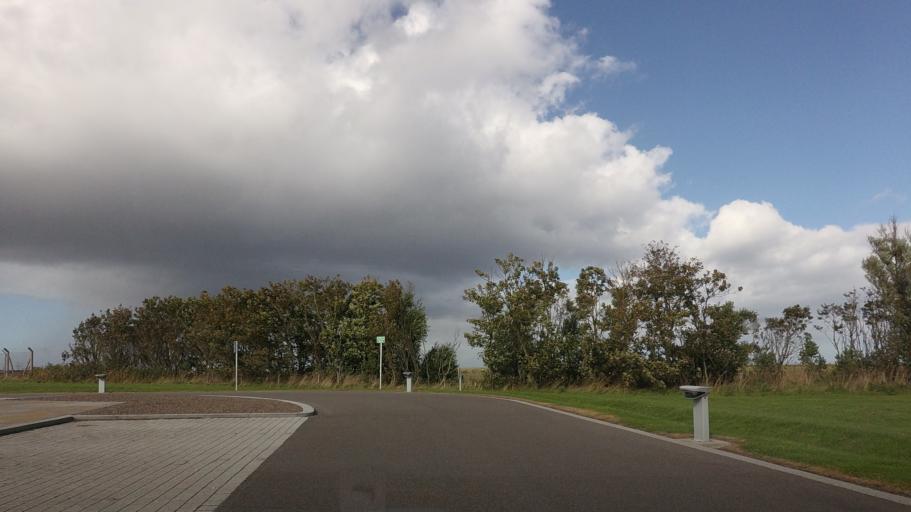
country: GB
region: Scotland
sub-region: Highland
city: Wick
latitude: 58.4527
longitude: -3.0845
